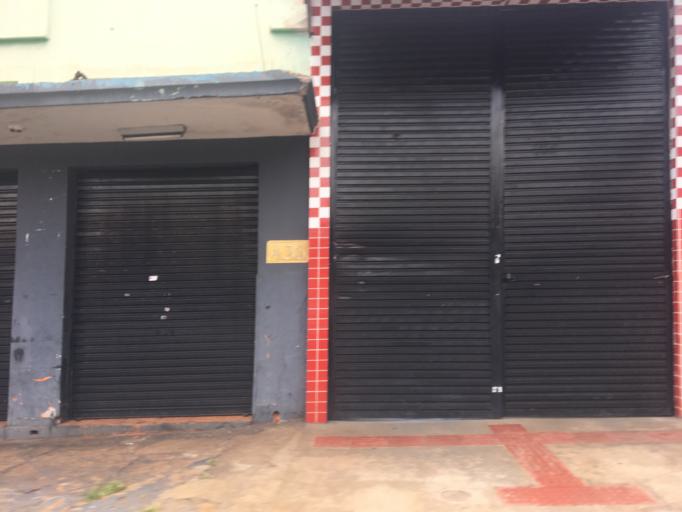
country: BR
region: Parana
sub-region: Londrina
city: Londrina
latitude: -23.3038
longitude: -51.1628
